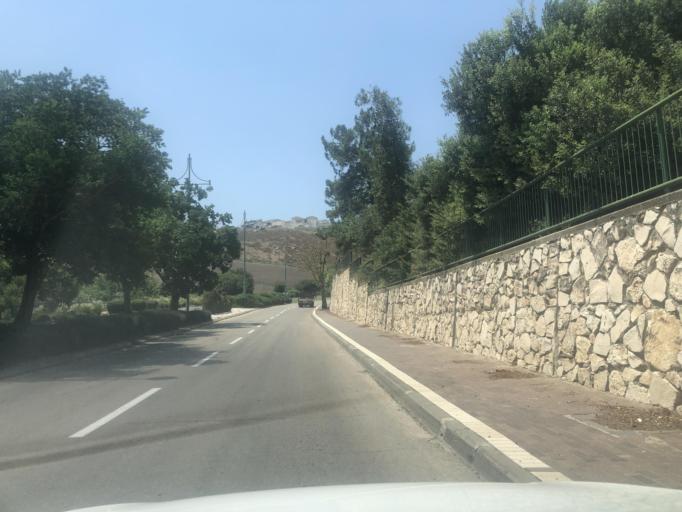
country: IL
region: Haifa
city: Daliyat el Karmil
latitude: 32.6512
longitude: 35.1035
